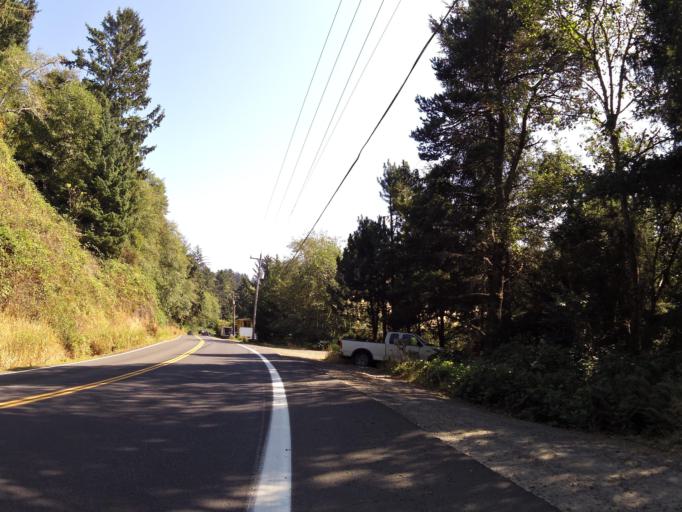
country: US
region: Oregon
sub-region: Tillamook County
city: Pacific City
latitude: 45.1915
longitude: -123.9545
